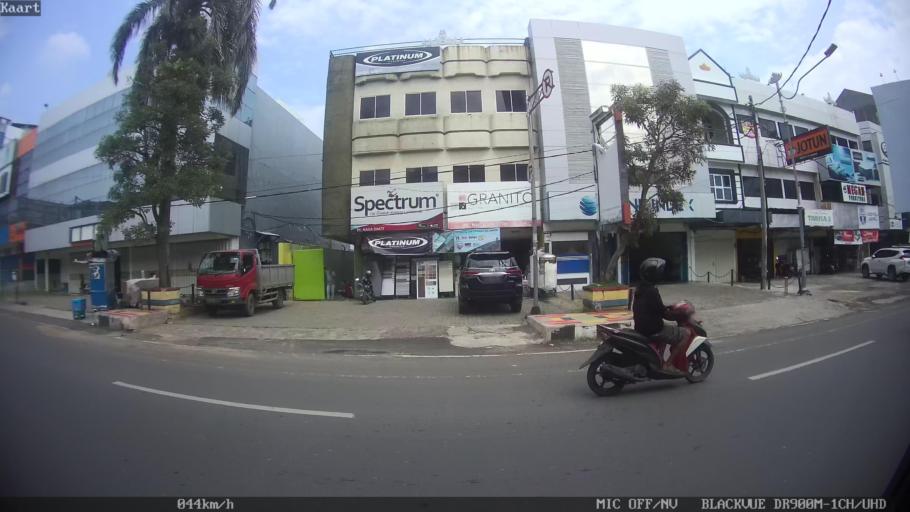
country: ID
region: Lampung
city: Bandarlampung
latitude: -5.4162
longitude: 105.2544
